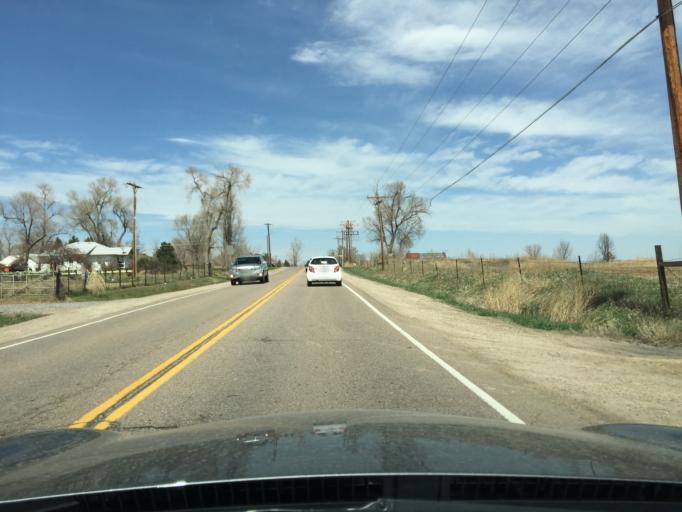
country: US
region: Colorado
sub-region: Adams County
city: Northglenn
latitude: 39.9707
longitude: -104.9971
